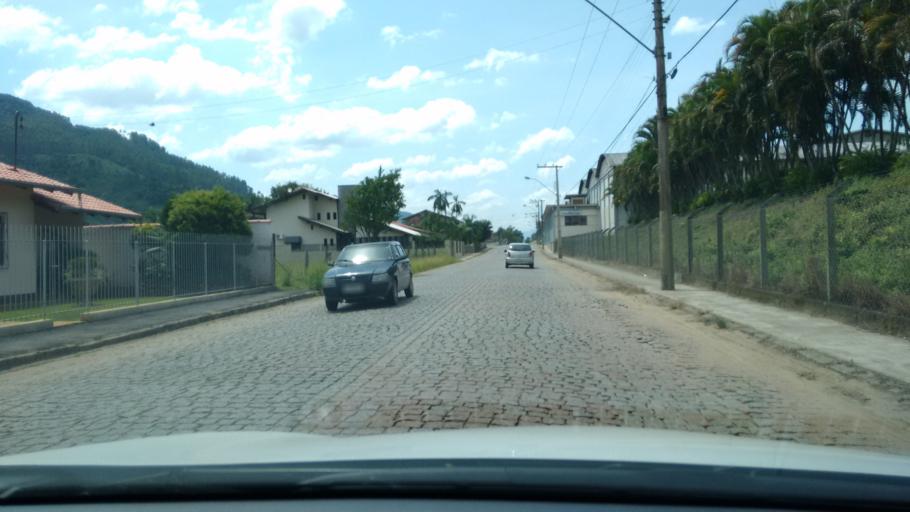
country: BR
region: Santa Catarina
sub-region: Rodeio
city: Gavea
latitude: -26.8688
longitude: -49.3377
